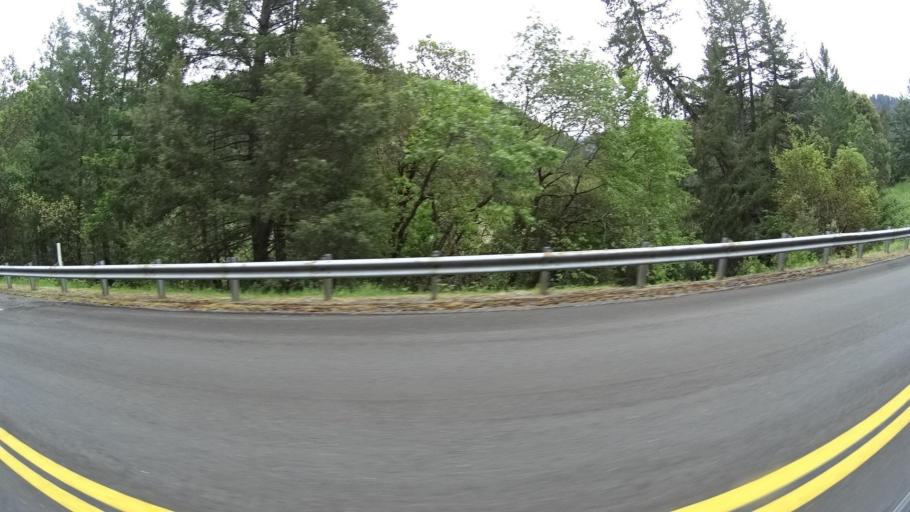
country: US
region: California
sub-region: Humboldt County
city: Willow Creek
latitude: 41.2840
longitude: -123.5759
